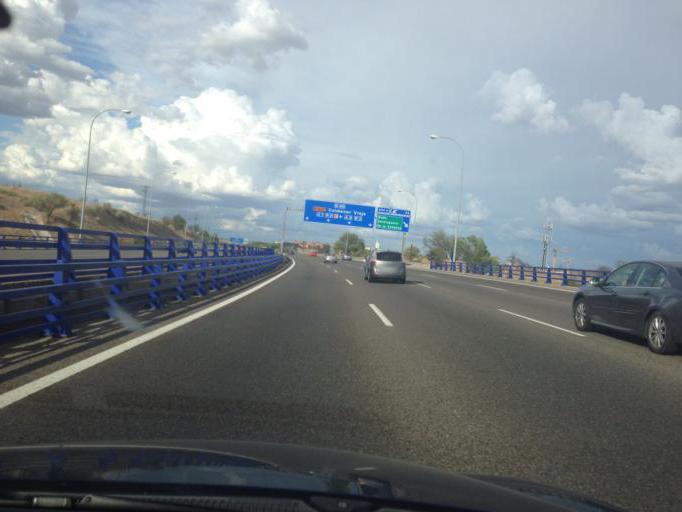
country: ES
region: Madrid
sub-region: Provincia de Madrid
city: Fuencarral-El Pardo
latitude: 40.4948
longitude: -3.7291
